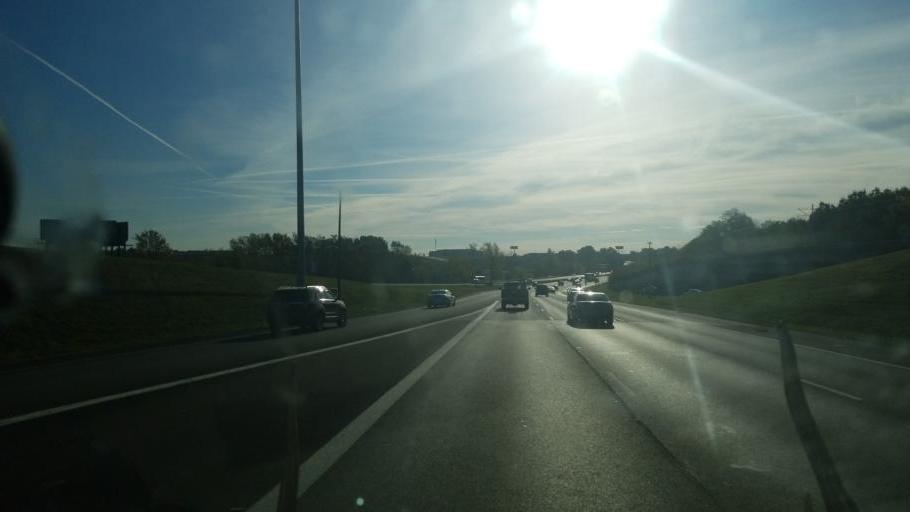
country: US
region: Missouri
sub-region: Saint Louis County
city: Bel-Ridge
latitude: 38.7277
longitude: -90.3300
